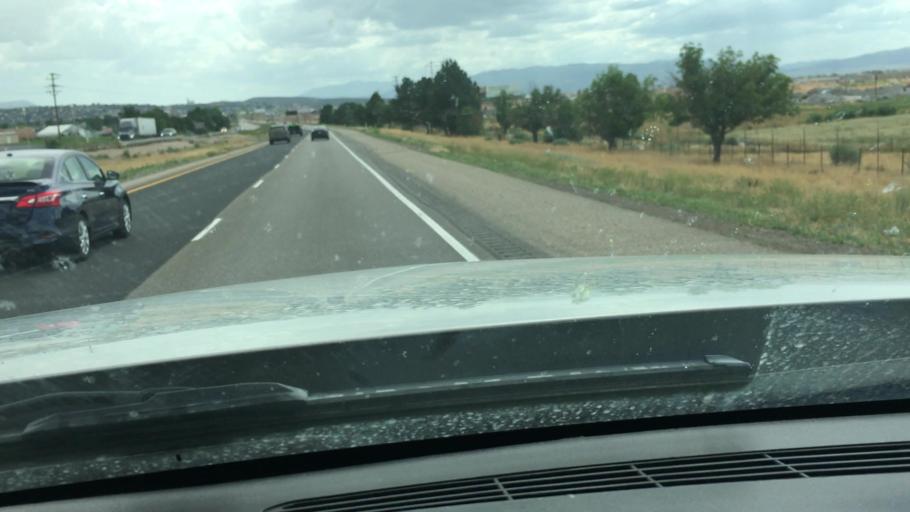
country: US
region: Utah
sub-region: Iron County
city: Cedar City
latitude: 37.7179
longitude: -113.0628
